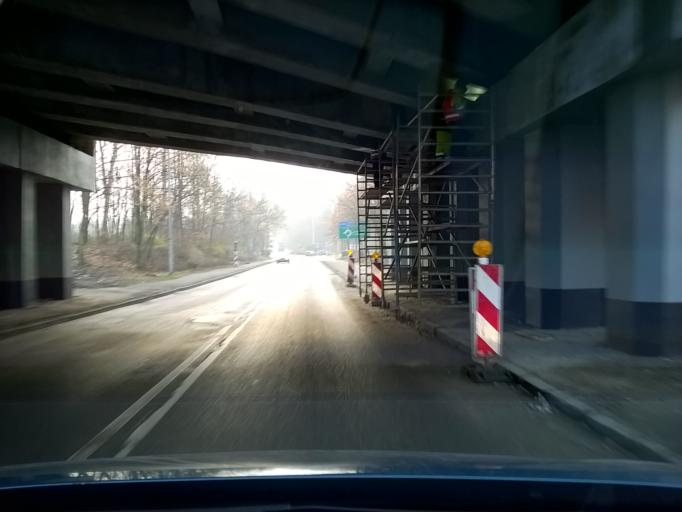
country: PL
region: Silesian Voivodeship
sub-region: Swietochlowice
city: Swietochlowice
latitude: 50.2603
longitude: 18.9359
